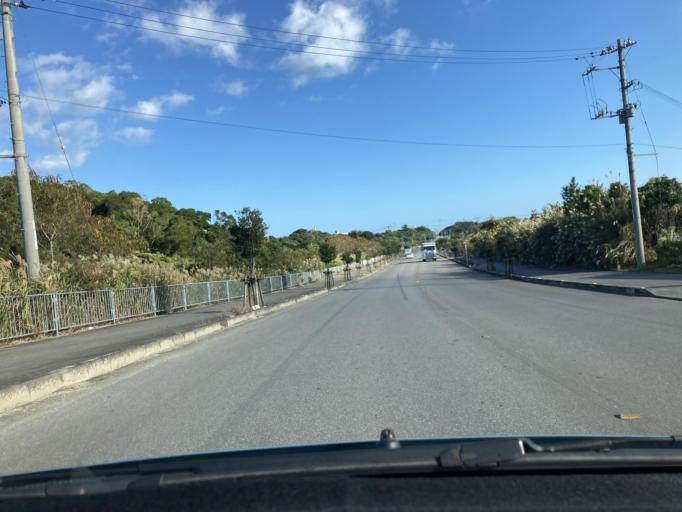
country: JP
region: Okinawa
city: Gushikawa
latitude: 26.3869
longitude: 127.8421
